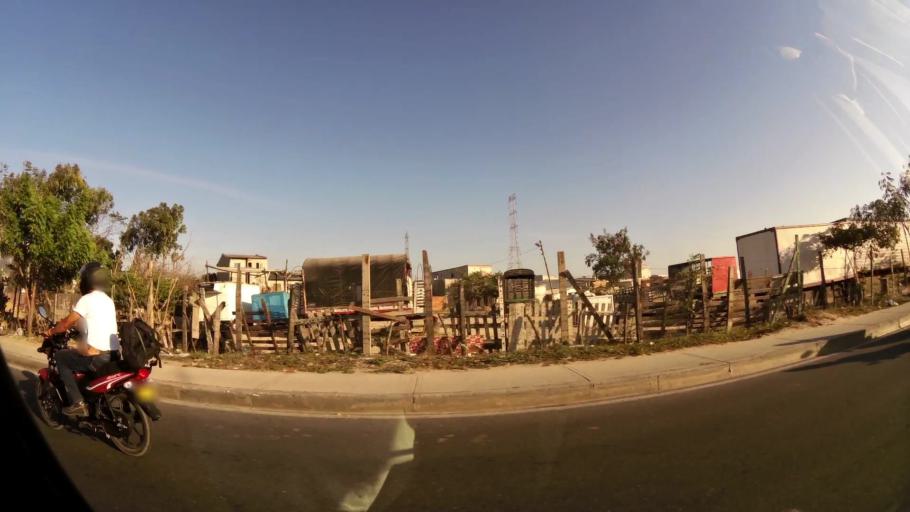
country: CO
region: Atlantico
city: Soledad
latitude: 10.9273
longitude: -74.7874
